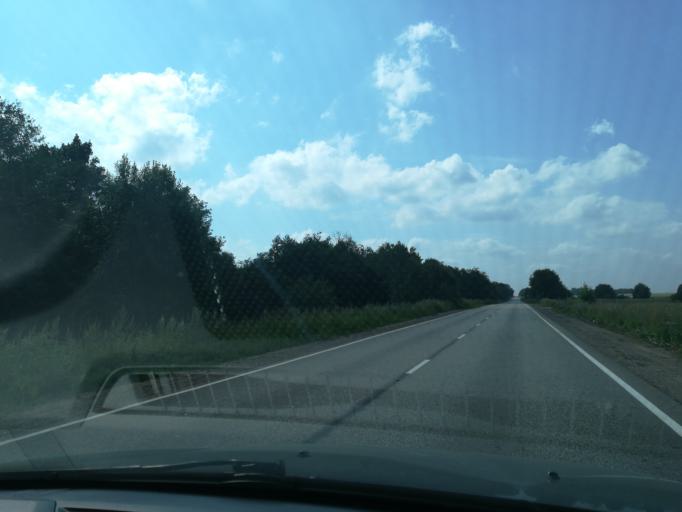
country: RU
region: Leningrad
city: Kopor'ye
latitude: 59.6641
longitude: 29.0297
